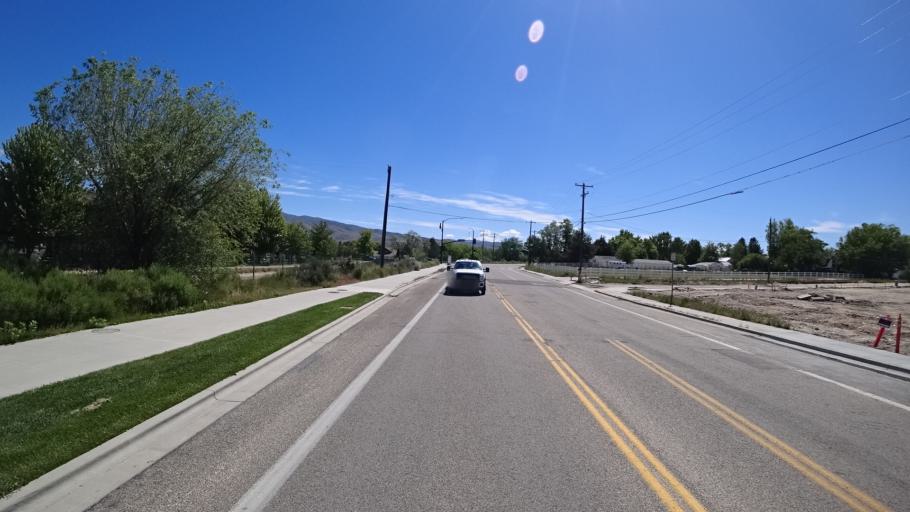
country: US
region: Idaho
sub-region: Ada County
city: Boise
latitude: 43.5734
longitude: -116.1570
